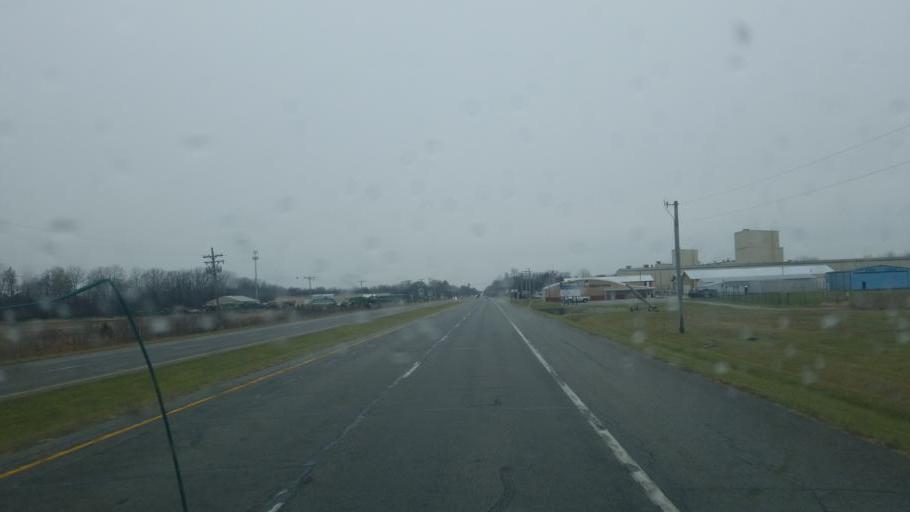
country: US
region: Indiana
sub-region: Hancock County
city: Greenfield
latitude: 39.7870
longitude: -85.7333
